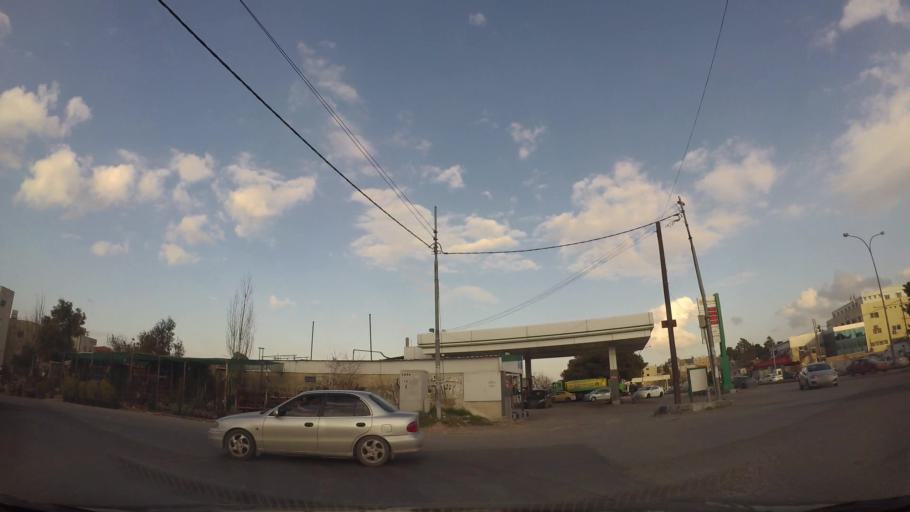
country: JO
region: Amman
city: Al Bunayyat ash Shamaliyah
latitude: 31.9104
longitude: 35.8906
